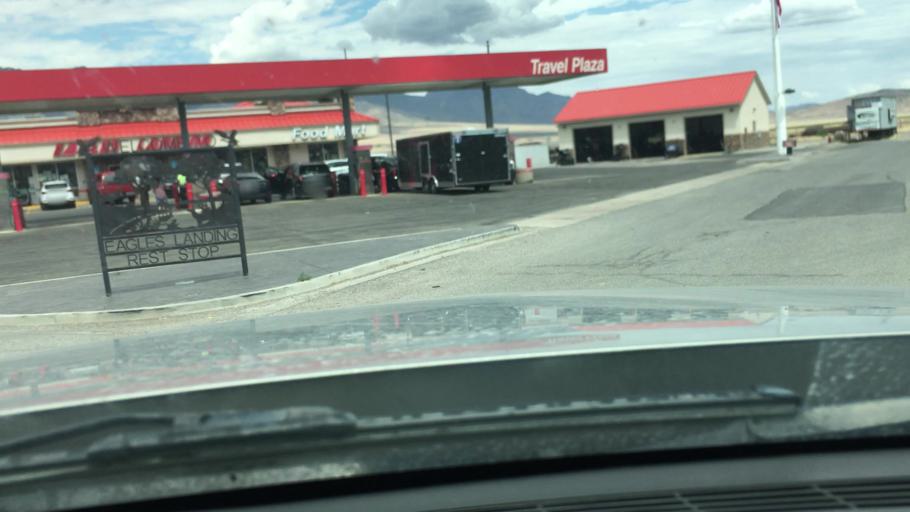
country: US
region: Utah
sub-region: Sanpete County
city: Gunnison
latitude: 39.2551
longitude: -112.1171
